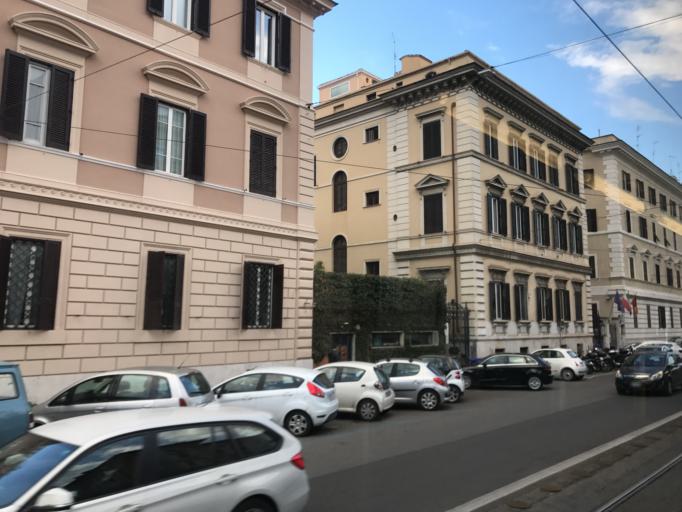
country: IT
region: Latium
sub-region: Citta metropolitana di Roma Capitale
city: Rome
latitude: 41.9120
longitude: 12.5079
